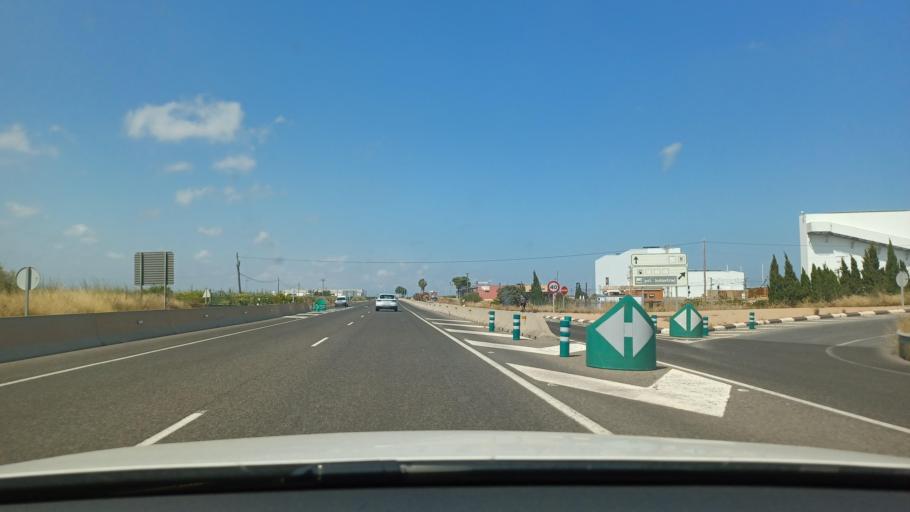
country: ES
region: Valencia
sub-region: Provincia de Castello
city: Chilches
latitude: 39.7974
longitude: -0.1793
